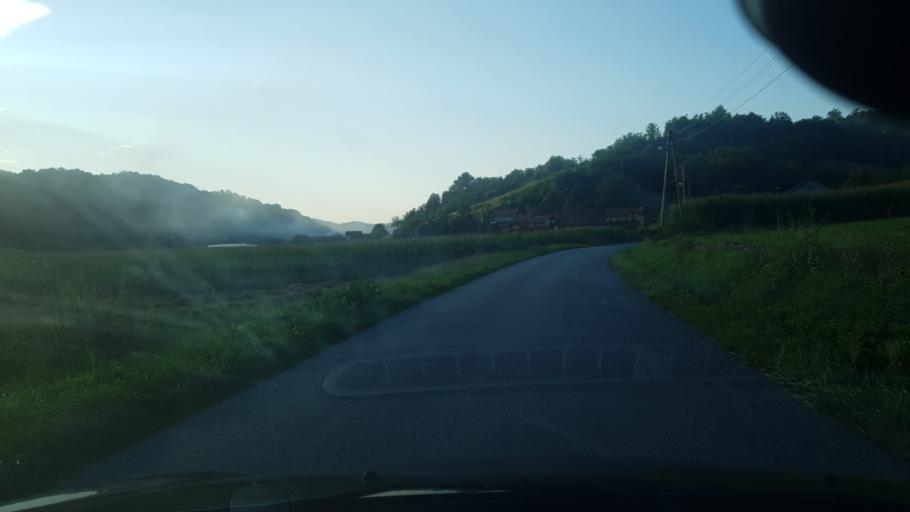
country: HR
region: Krapinsko-Zagorska
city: Zabok
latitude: 46.0877
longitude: 15.8858
